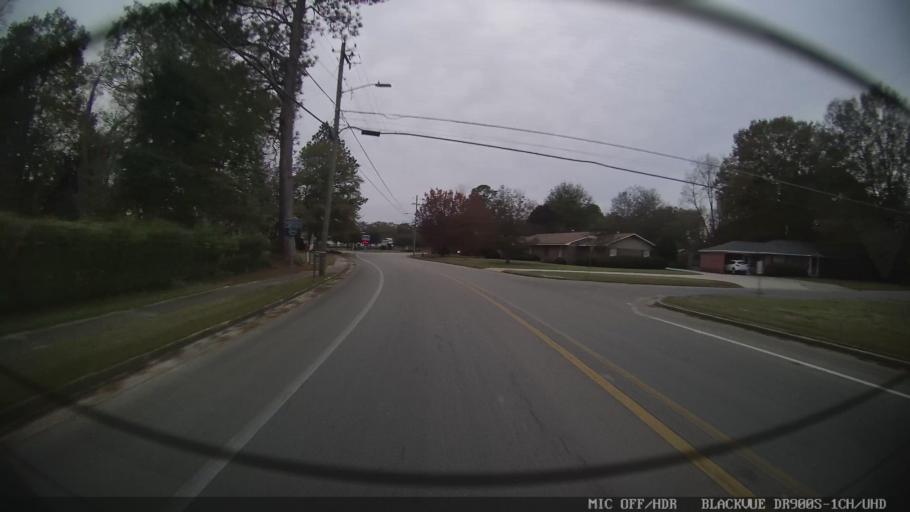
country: US
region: Mississippi
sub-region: Clarke County
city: Quitman
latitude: 32.0376
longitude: -88.7198
